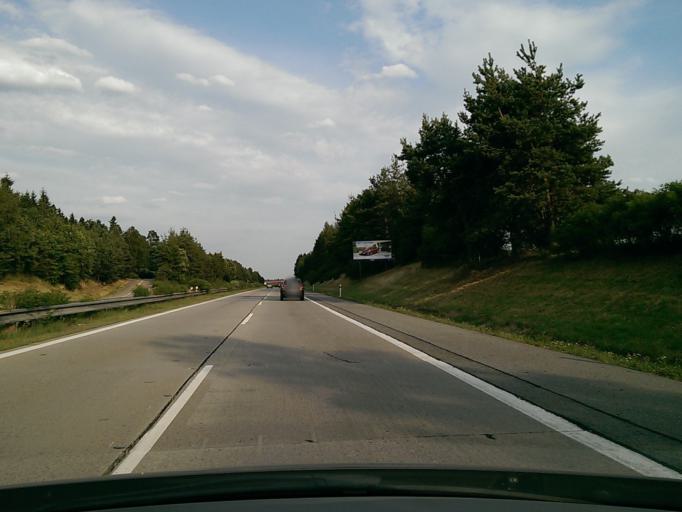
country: CZ
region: Vysocina
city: Dobronin
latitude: 49.4387
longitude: 15.6390
